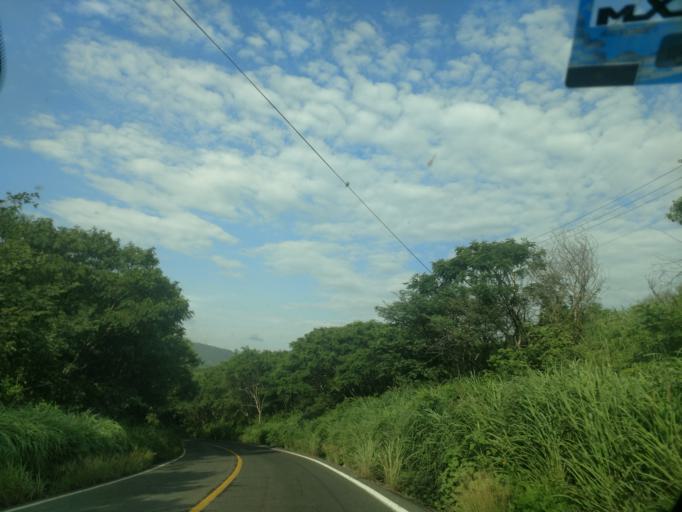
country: MX
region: Jalisco
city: Ameca
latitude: 20.5229
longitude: -104.1233
